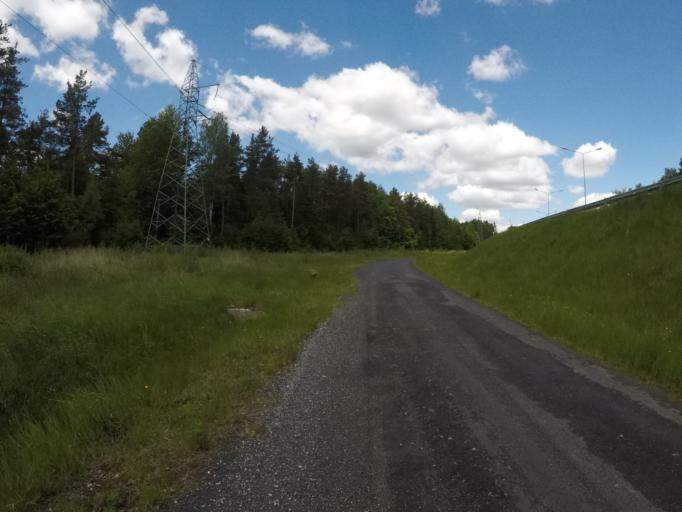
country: PL
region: Swietokrzyskie
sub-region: Powiat kielecki
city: Zagnansk
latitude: 50.9393
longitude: 20.6693
